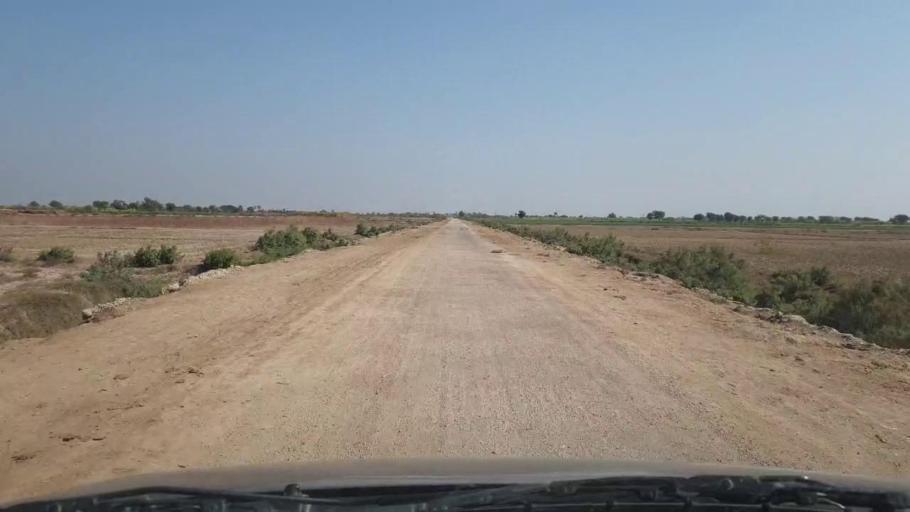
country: PK
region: Sindh
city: Samaro
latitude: 25.1983
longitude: 69.2932
